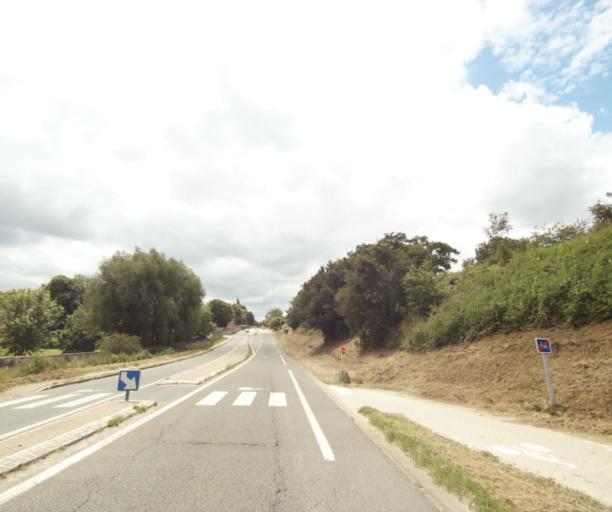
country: FR
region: Ile-de-France
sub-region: Departement des Yvelines
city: Bailly
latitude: 48.8194
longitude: 2.0810
